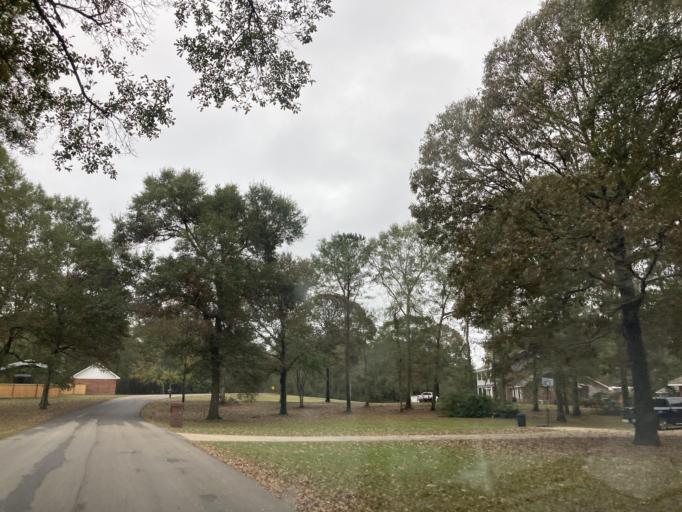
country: US
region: Mississippi
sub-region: Lamar County
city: Purvis
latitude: 31.1599
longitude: -89.4232
